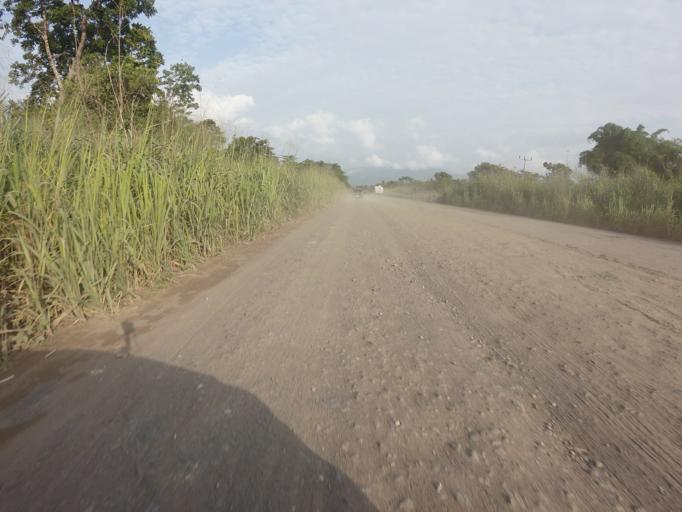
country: GH
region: Volta
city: Kpandu
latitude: 6.9747
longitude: 0.4507
